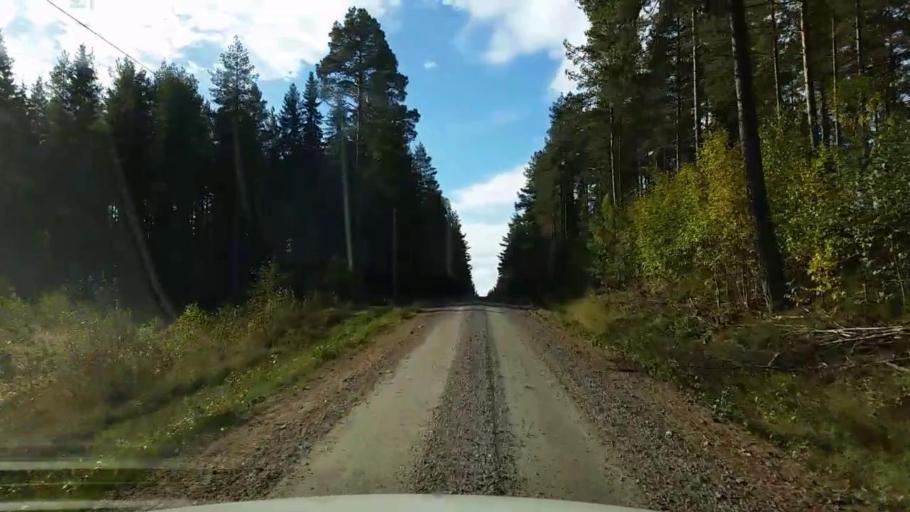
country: SE
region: Gaevleborg
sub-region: Ljusdals Kommun
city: Jaervsoe
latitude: 61.7892
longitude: 16.1714
